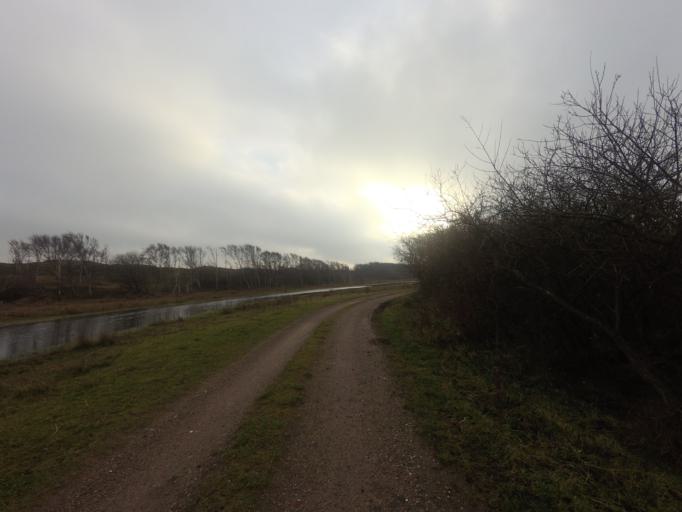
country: NL
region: North Holland
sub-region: Gemeente Texel
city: Den Burg
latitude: 53.1193
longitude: 4.7979
